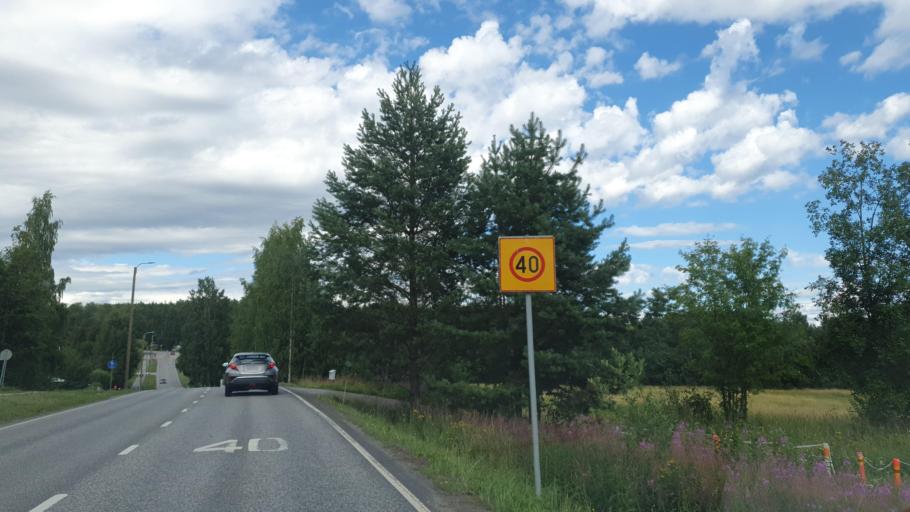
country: FI
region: Central Finland
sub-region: Jyvaeskylae
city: Saeynaetsalo
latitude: 62.1526
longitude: 25.7540
